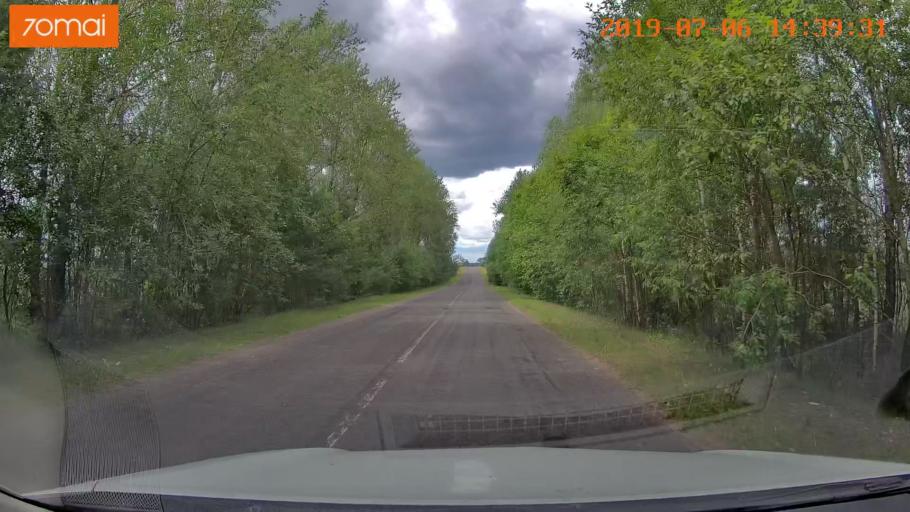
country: BY
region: Minsk
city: Ivyanyets
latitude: 53.9172
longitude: 26.6877
